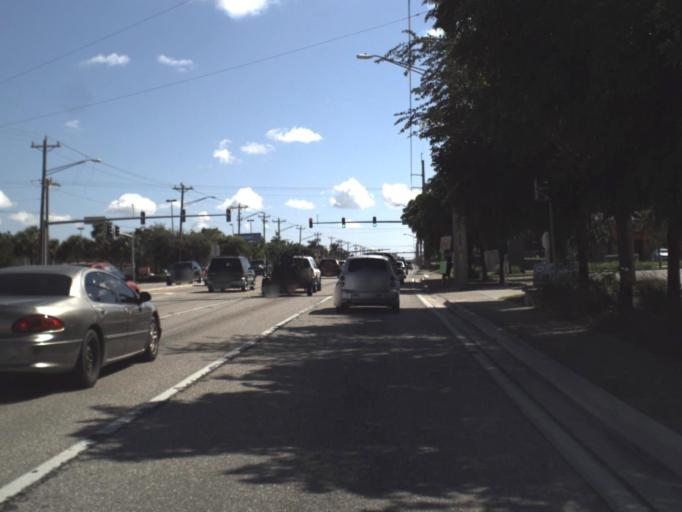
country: US
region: Florida
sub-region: Lee County
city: Lochmoor Waterway Estates
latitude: 26.6231
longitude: -81.9409
